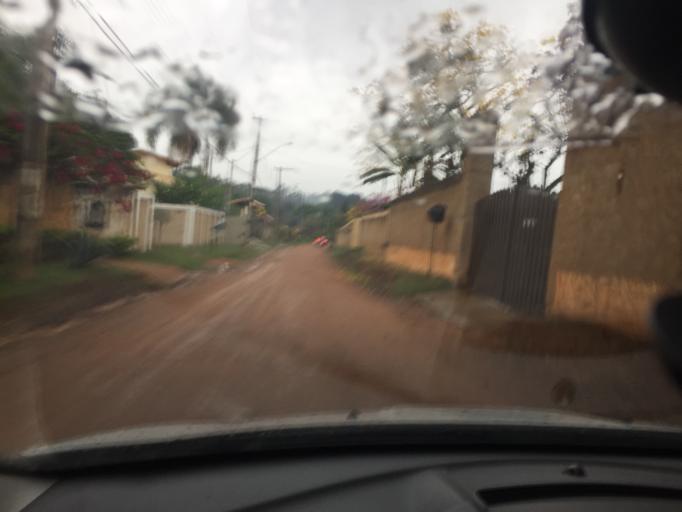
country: BR
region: Sao Paulo
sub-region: Jarinu
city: Jarinu
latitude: -23.1365
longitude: -46.7209
